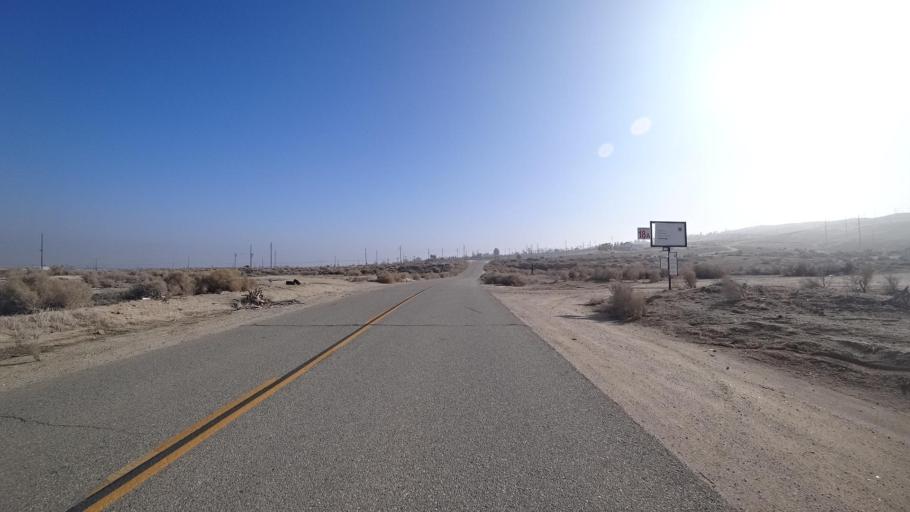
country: US
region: California
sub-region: Kern County
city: Taft Heights
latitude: 35.1399
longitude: -119.4885
